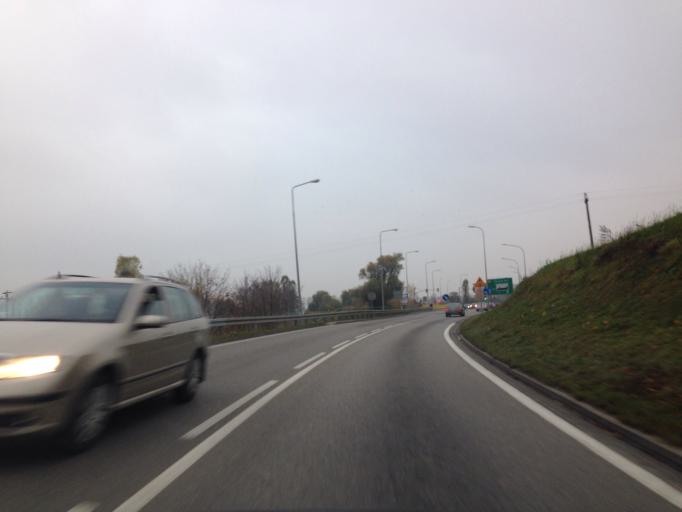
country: PL
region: Pomeranian Voivodeship
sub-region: Powiat gdanski
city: Pruszcz Gdanski
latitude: 54.2721
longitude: 18.6381
